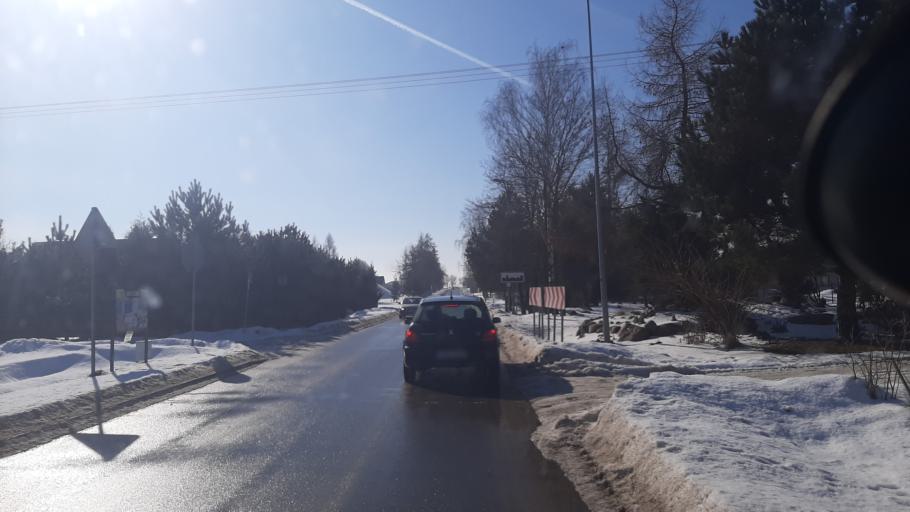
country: PL
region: Lublin Voivodeship
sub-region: Powiat lubelski
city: Garbow
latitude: 51.3090
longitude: 22.3067
